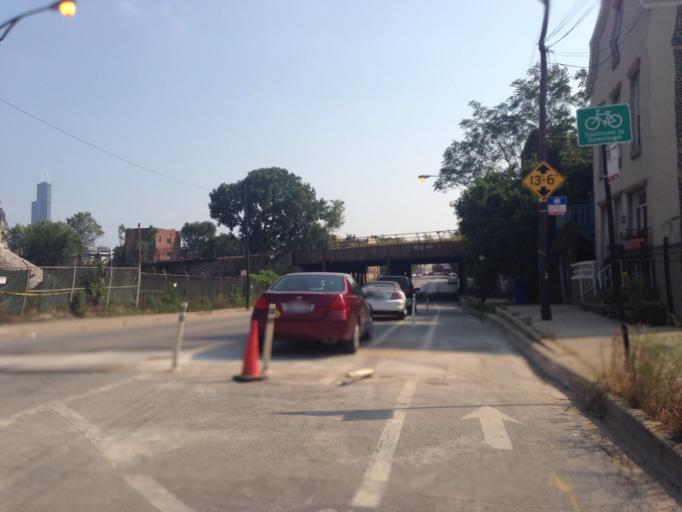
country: US
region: Illinois
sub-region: Cook County
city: Chicago
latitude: 41.8999
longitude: -87.6567
